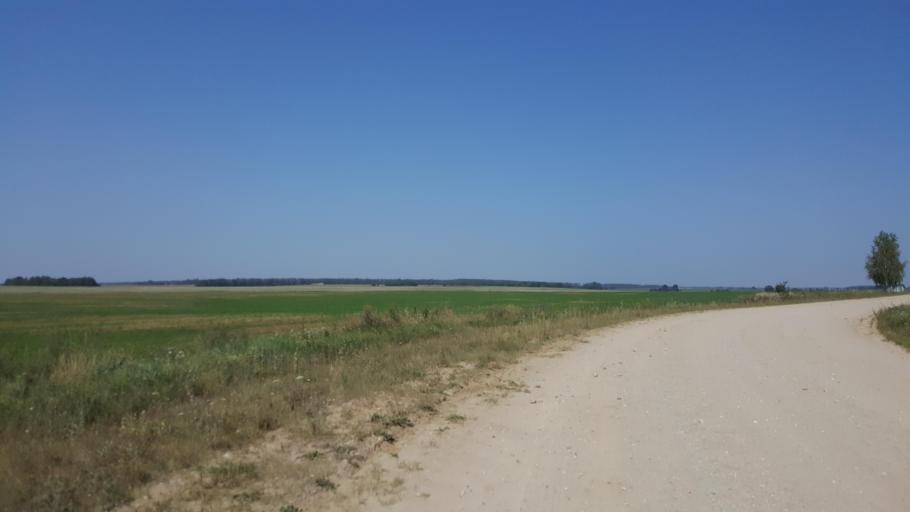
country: BY
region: Brest
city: Vysokaye
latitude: 52.4507
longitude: 23.4449
